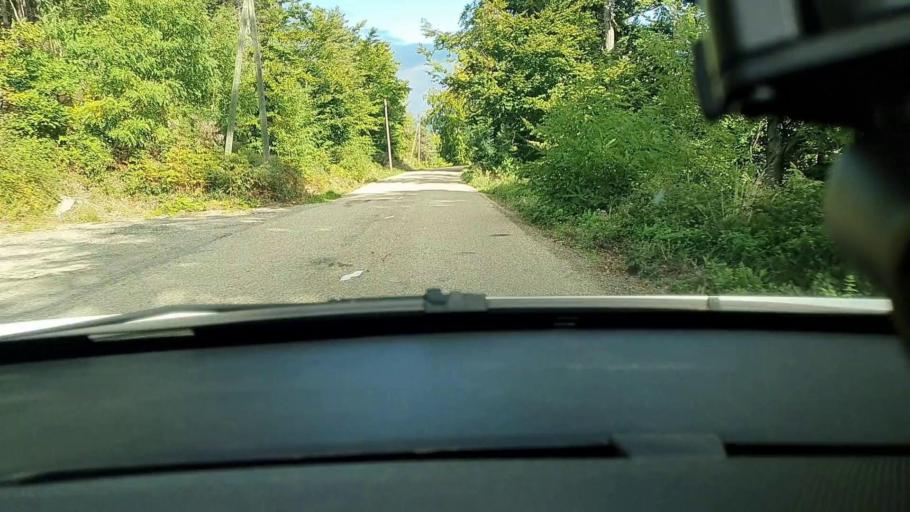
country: FR
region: Rhone-Alpes
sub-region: Departement de l'Ardeche
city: Les Vans
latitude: 44.4269
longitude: 4.0232
